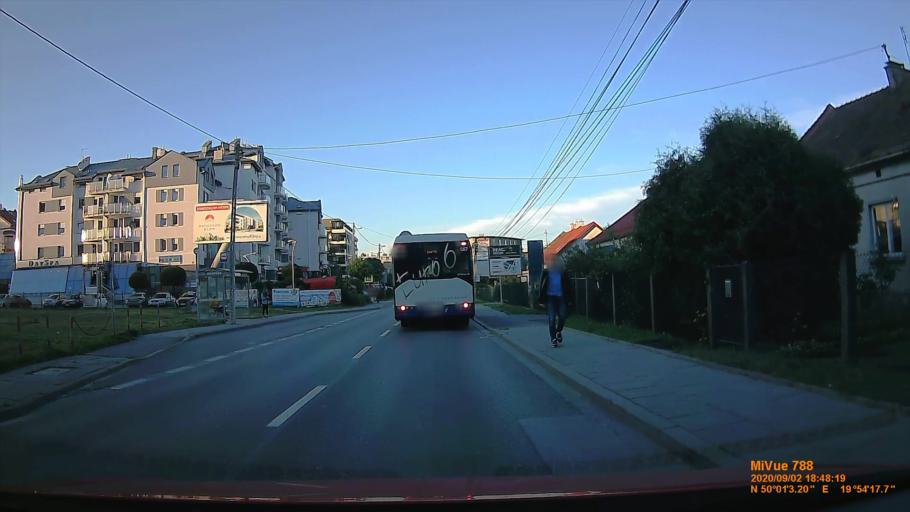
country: PL
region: Lesser Poland Voivodeship
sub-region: Krakow
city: Sidzina
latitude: 50.0177
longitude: 19.9051
